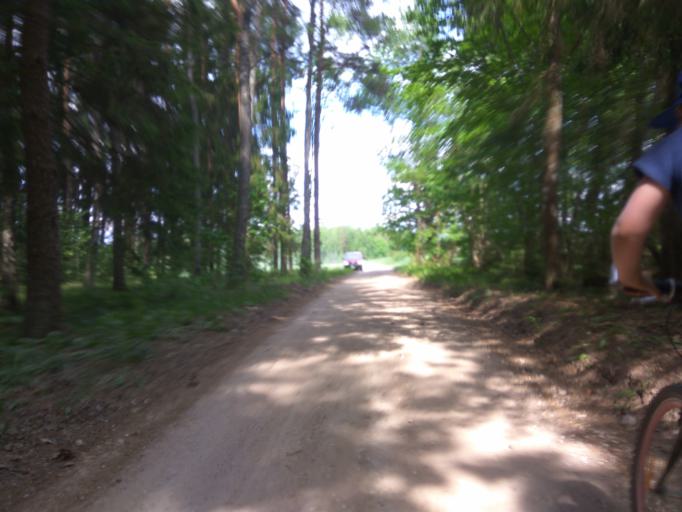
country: LV
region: Kuldigas Rajons
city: Kuldiga
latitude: 56.9010
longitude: 21.9241
